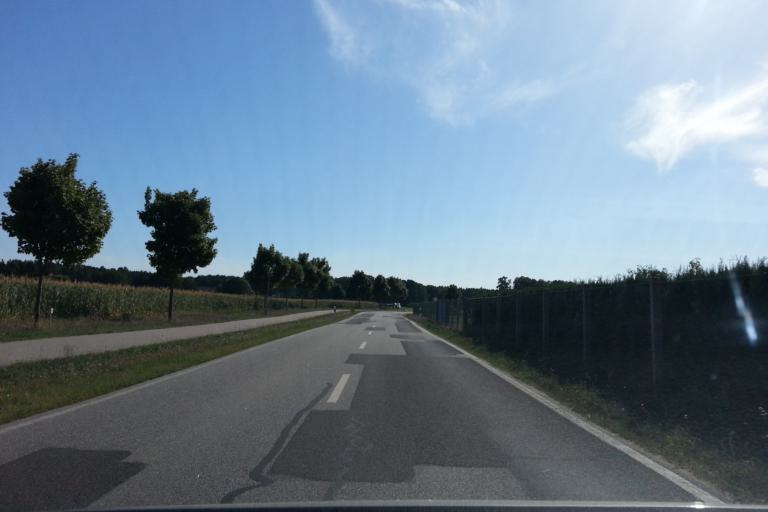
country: DE
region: Mecklenburg-Vorpommern
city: Eggesin
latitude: 53.6791
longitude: 14.0368
